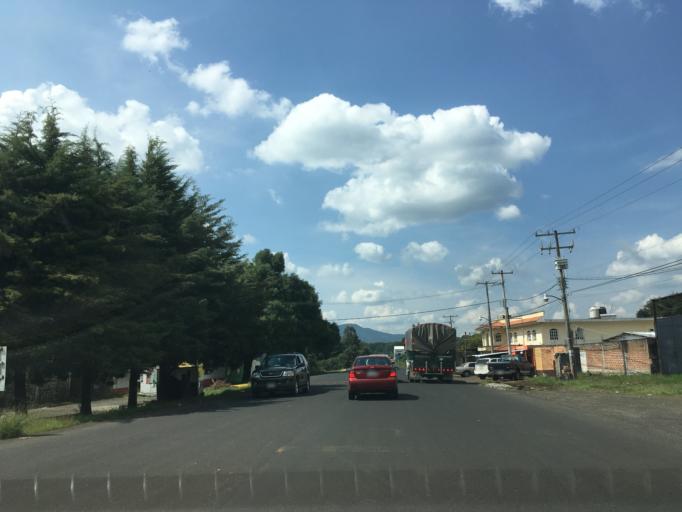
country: MX
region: Michoacan
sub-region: Tingueindin
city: Tingueindin
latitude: 19.7733
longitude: -102.4999
